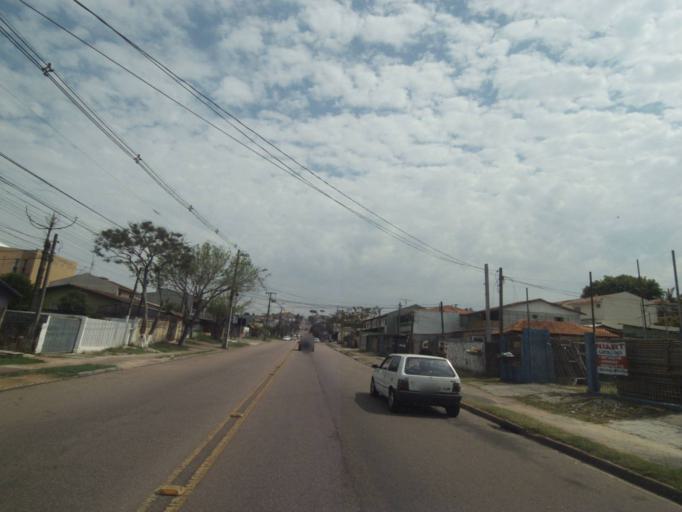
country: BR
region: Parana
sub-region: Pinhais
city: Pinhais
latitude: -25.4077
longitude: -49.2034
